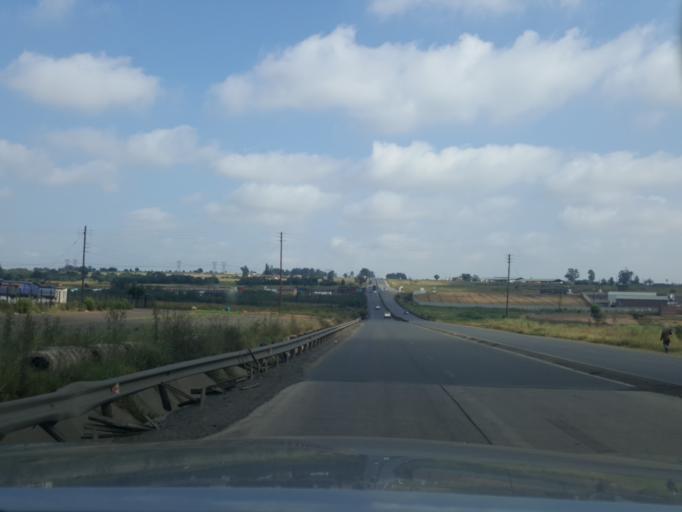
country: ZA
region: Mpumalanga
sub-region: Nkangala District Municipality
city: Witbank
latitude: -25.9612
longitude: 29.2599
